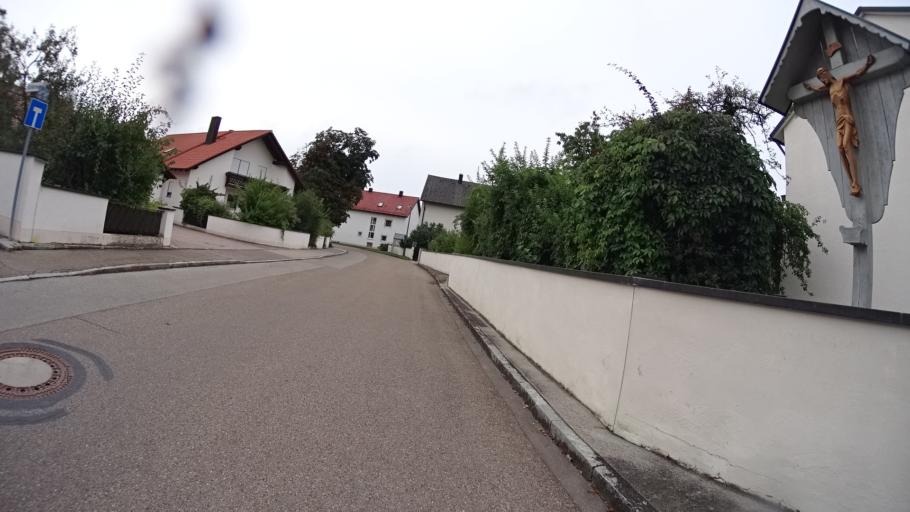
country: DE
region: Bavaria
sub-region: Upper Bavaria
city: Gaimersheim
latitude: 48.8350
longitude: 11.3566
